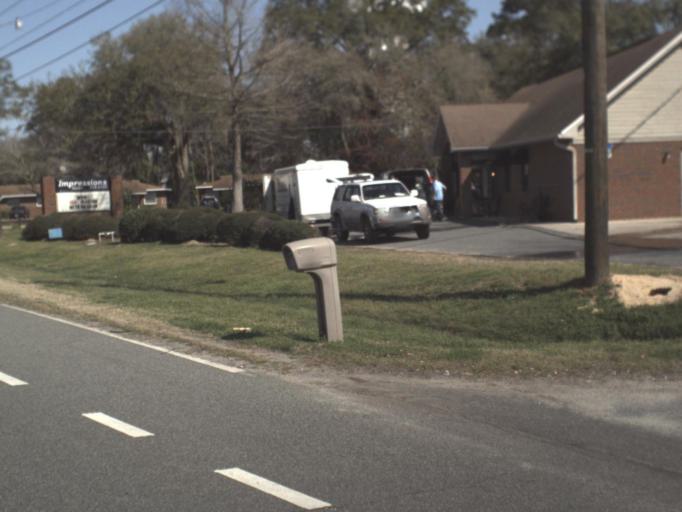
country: US
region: Florida
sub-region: Leon County
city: Tallahassee
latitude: 30.4908
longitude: -84.3230
